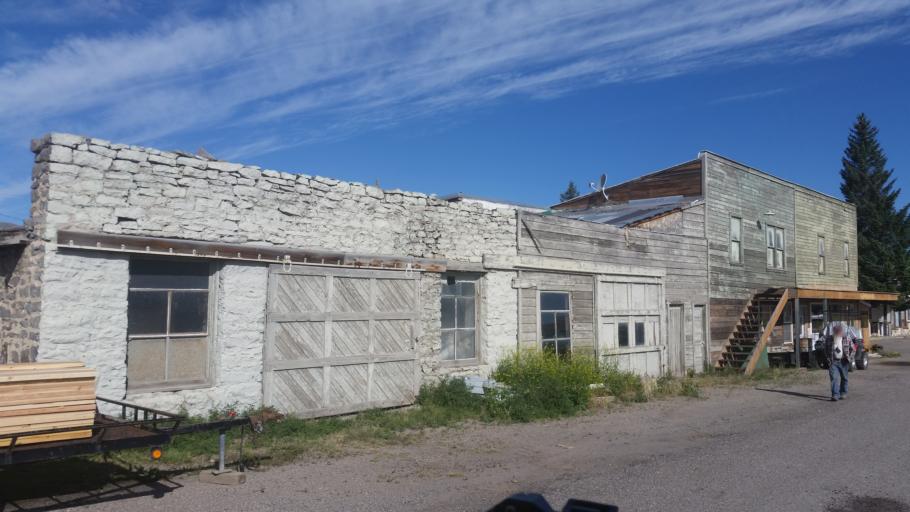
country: US
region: Montana
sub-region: Beaverhead County
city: Dillon
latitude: 44.6355
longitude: -112.5910
